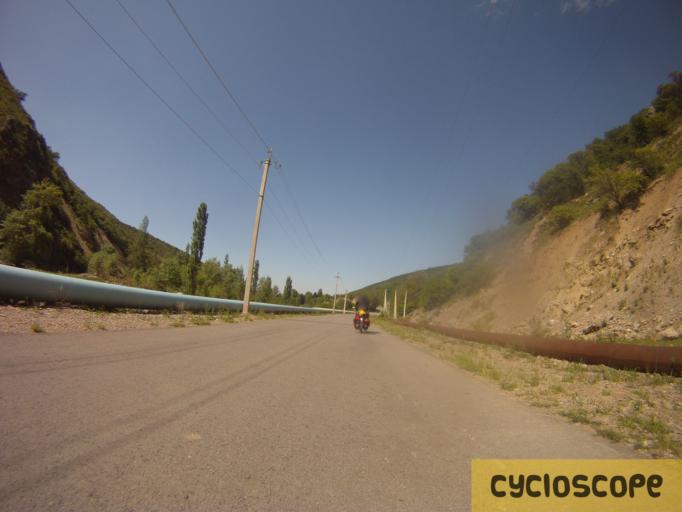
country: KZ
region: Almaty Oblysy
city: Esik
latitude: 43.2967
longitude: 77.4996
